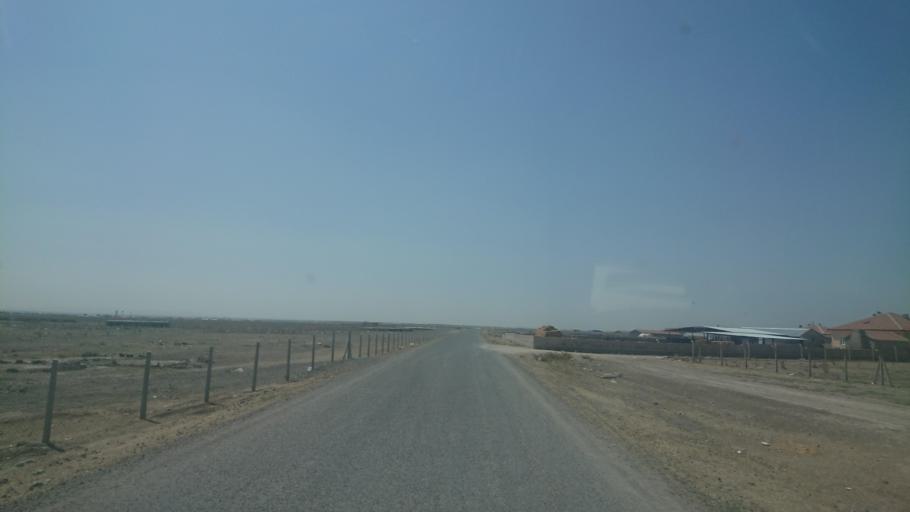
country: TR
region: Aksaray
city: Yesilova
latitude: 38.3313
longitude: 33.7498
